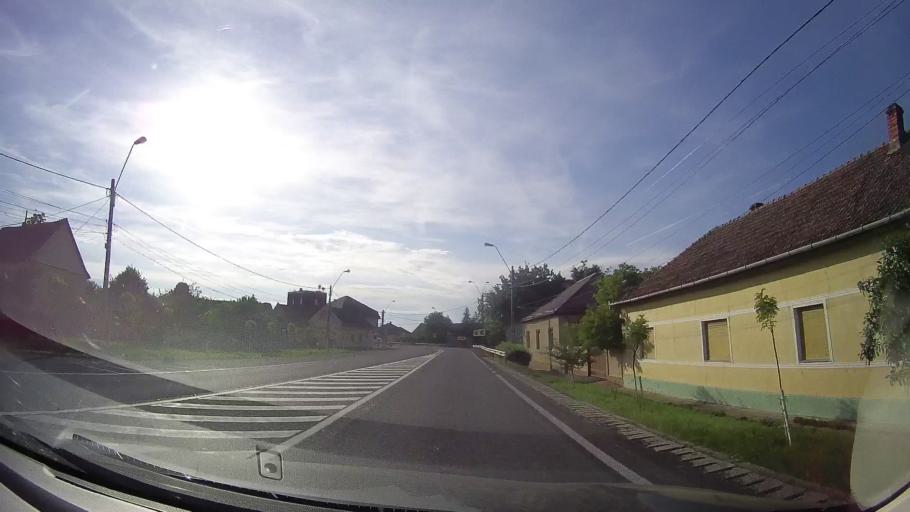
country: RO
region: Timis
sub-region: Oras Recas
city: Recas
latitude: 45.8001
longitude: 21.5134
